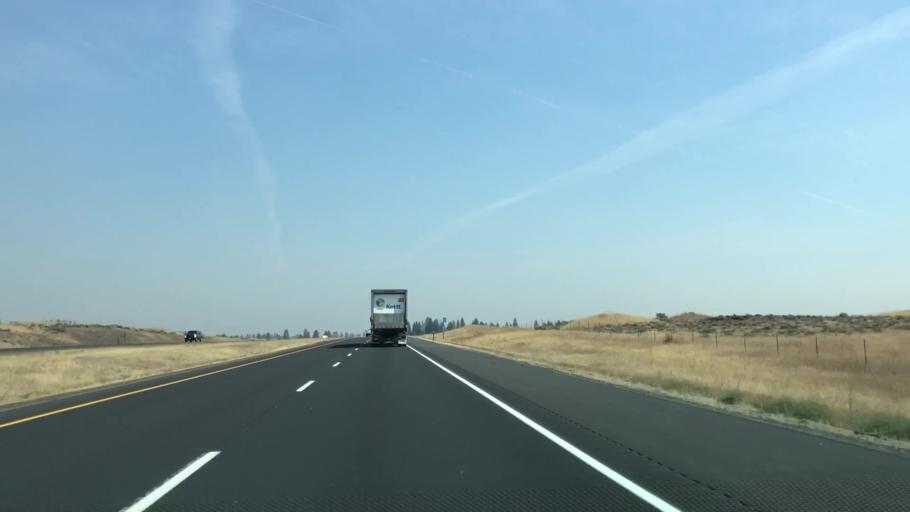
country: US
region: Washington
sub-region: Spokane County
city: Medical Lake
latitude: 47.3839
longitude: -117.8580
